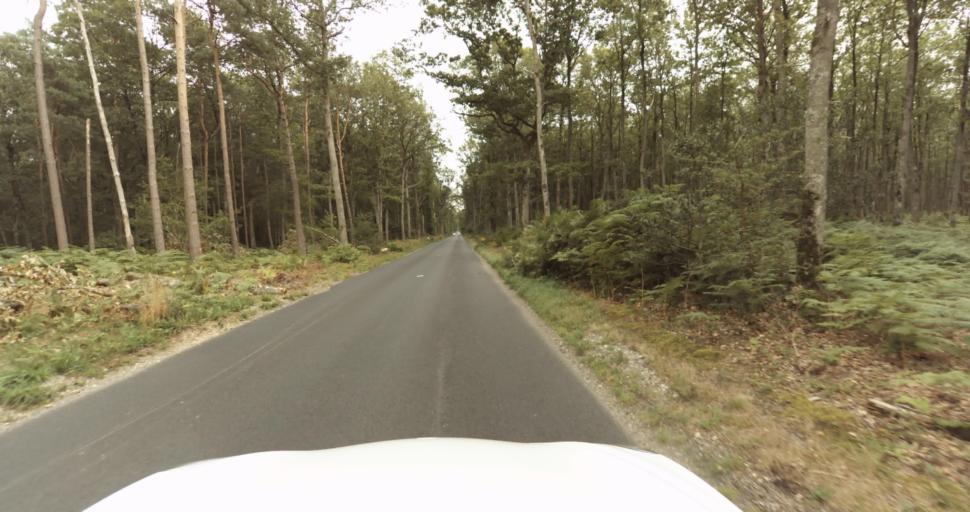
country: FR
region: Haute-Normandie
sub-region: Departement de l'Eure
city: Saint-Sebastien-de-Morsent
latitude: 48.9827
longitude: 1.0693
